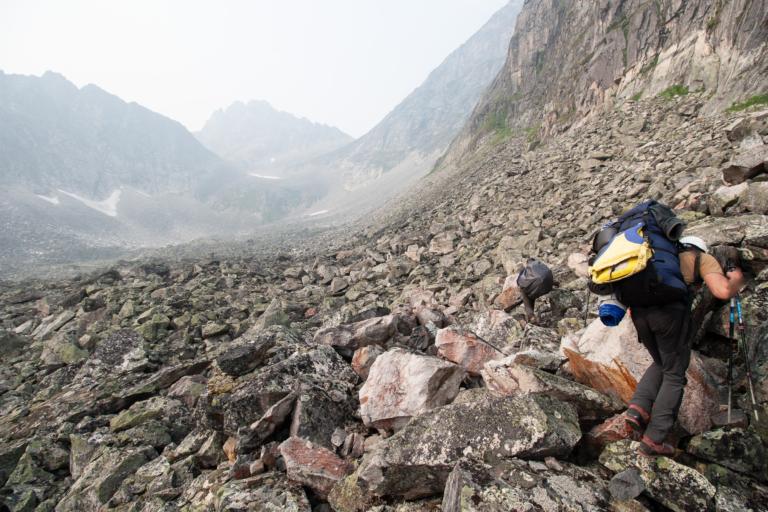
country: RU
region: Respublika Buryatiya
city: Kichera
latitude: 56.2213
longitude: 110.8714
